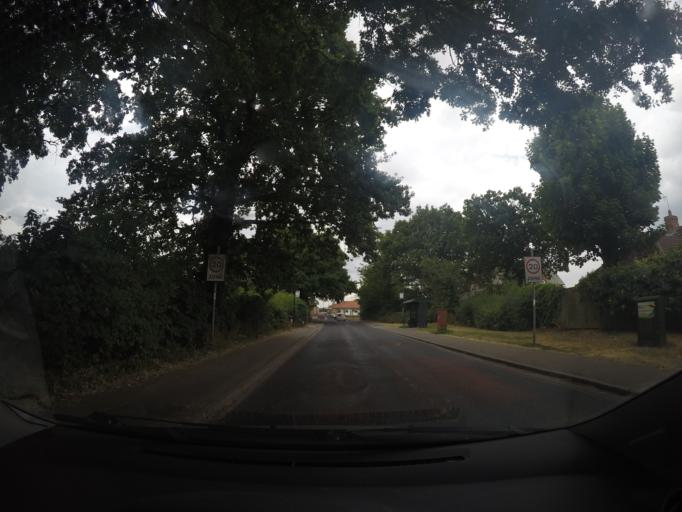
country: GB
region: England
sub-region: City of York
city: Huntington
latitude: 53.9939
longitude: -1.0588
